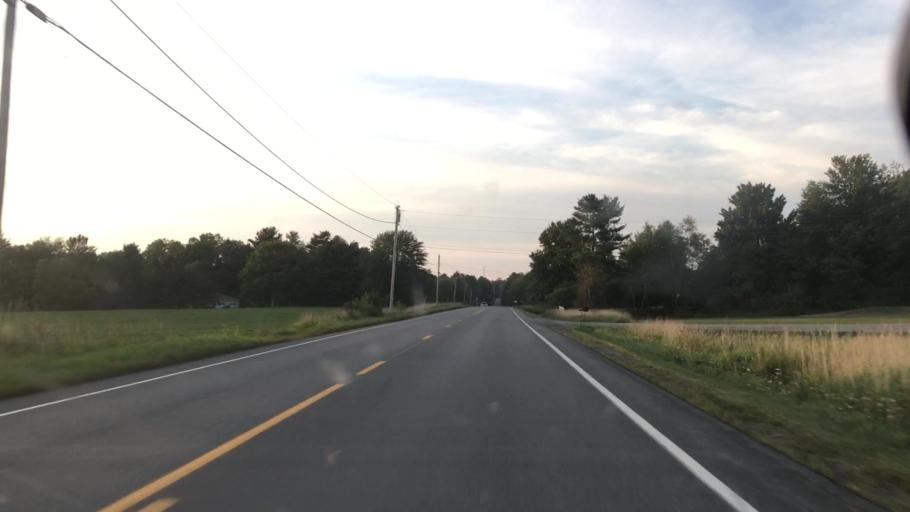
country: US
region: Maine
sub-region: Penobscot County
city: Hermon
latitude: 44.7467
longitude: -68.9675
